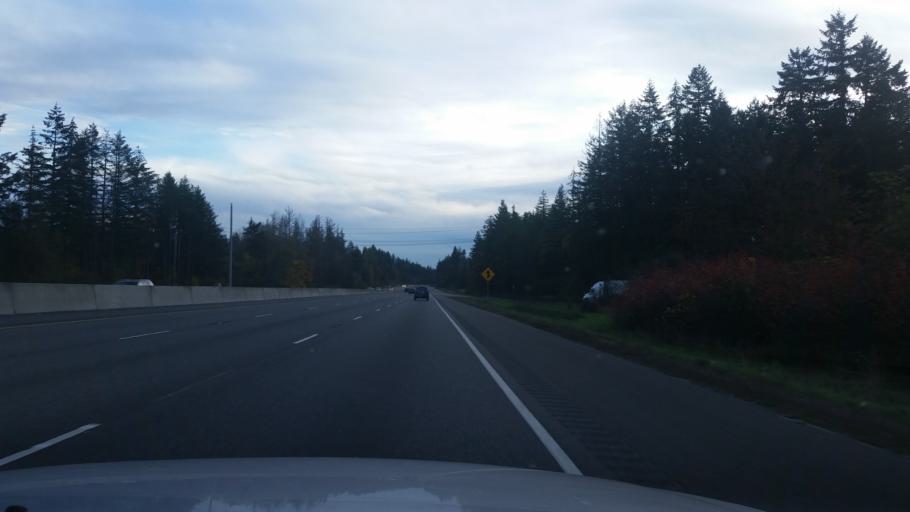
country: US
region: Washington
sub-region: Thurston County
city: Grand Mound
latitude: 46.8707
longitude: -122.9693
